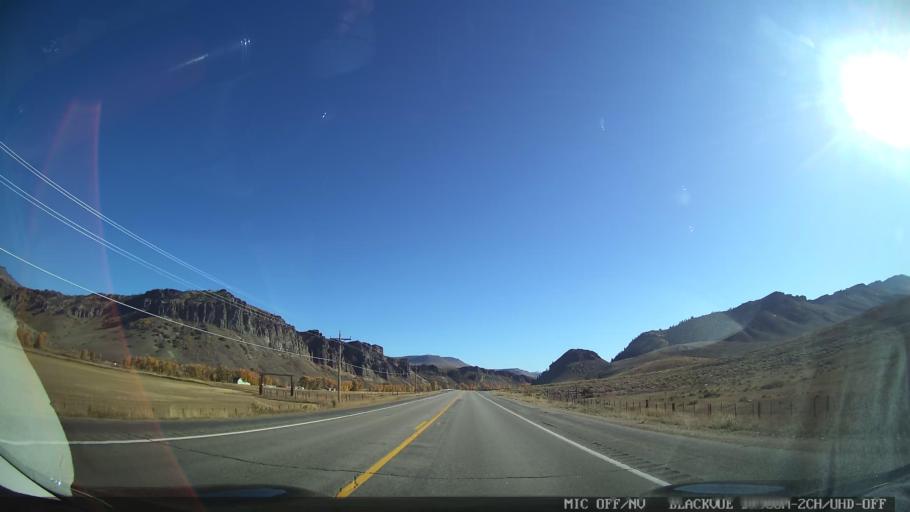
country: US
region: Colorado
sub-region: Grand County
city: Hot Sulphur Springs
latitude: 40.0781
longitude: -106.0924
